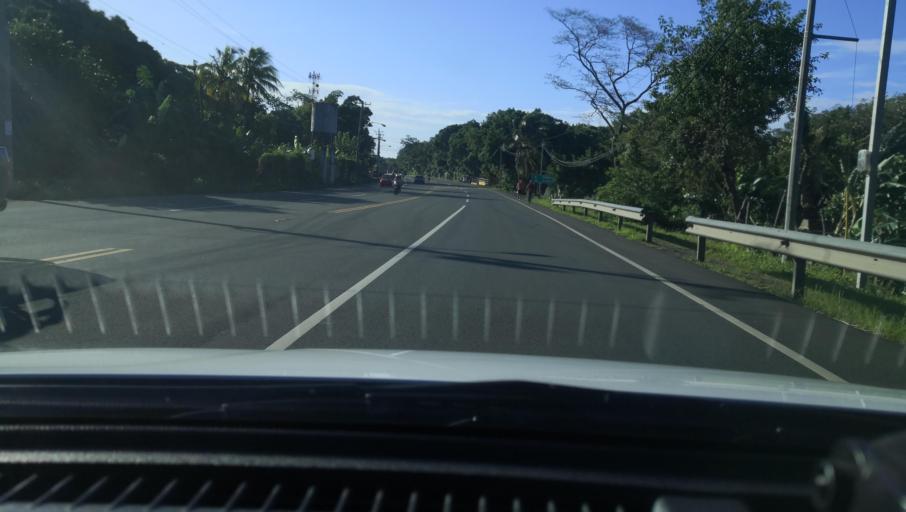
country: NI
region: Carazo
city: Jinotepe
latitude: 11.8289
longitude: -86.1752
